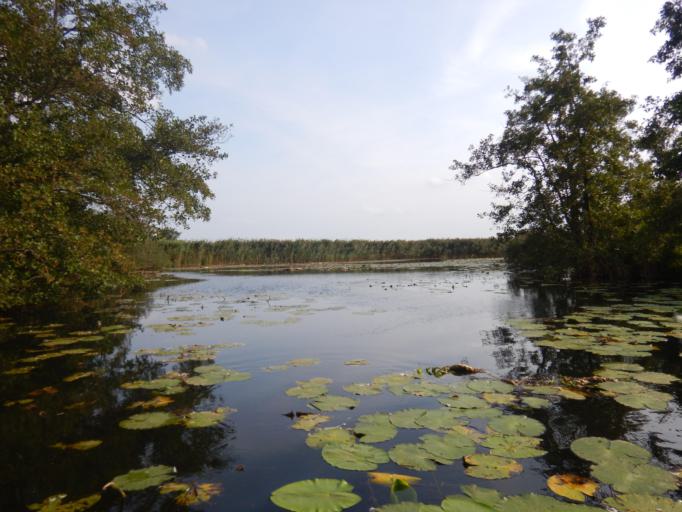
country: NL
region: South Holland
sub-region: Bodegraven-Reeuwijk
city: Bodegraven
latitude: 52.1164
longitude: 4.7533
